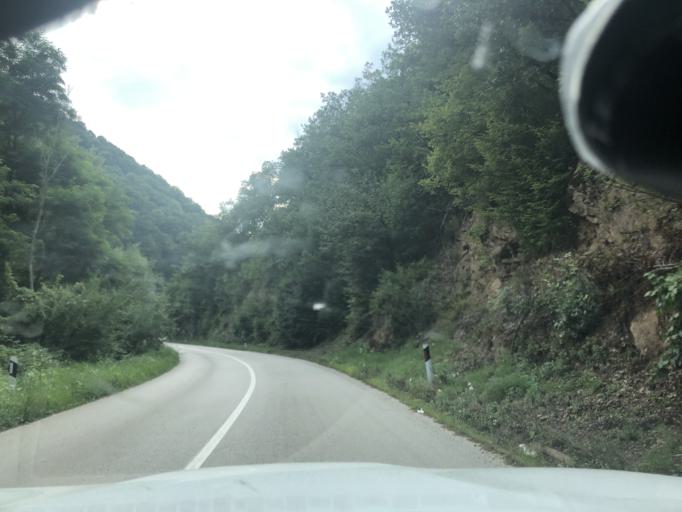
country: RS
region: Central Serbia
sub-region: Jablanicki Okrug
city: Medvega
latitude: 42.7814
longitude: 21.5955
